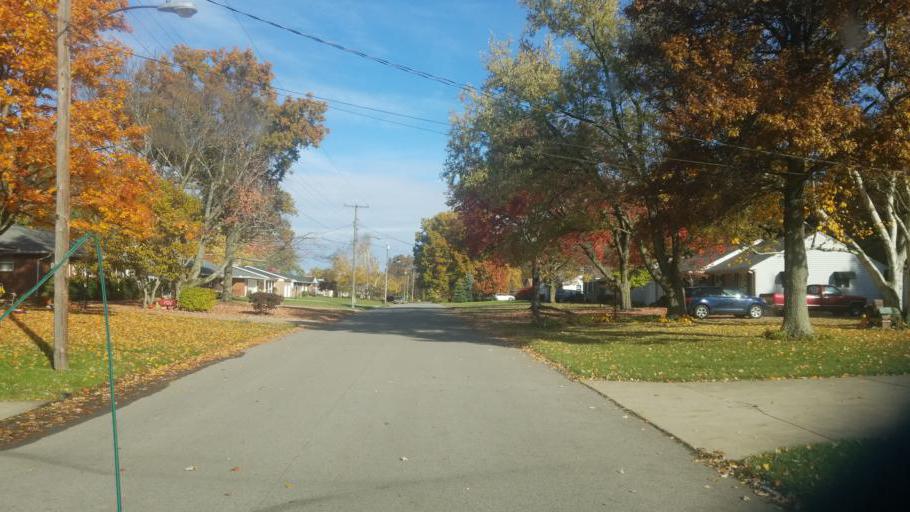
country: US
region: Ohio
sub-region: Richland County
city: Mansfield
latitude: 40.7303
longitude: -82.5243
